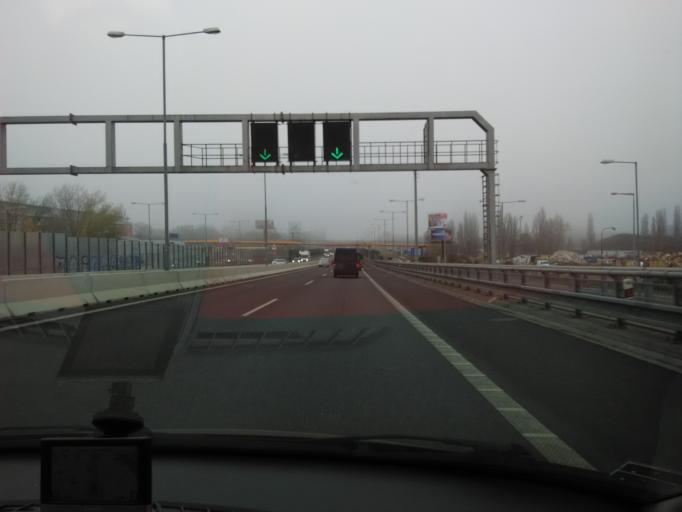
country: SK
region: Bratislavsky
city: Bratislava
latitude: 48.1312
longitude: 17.1260
